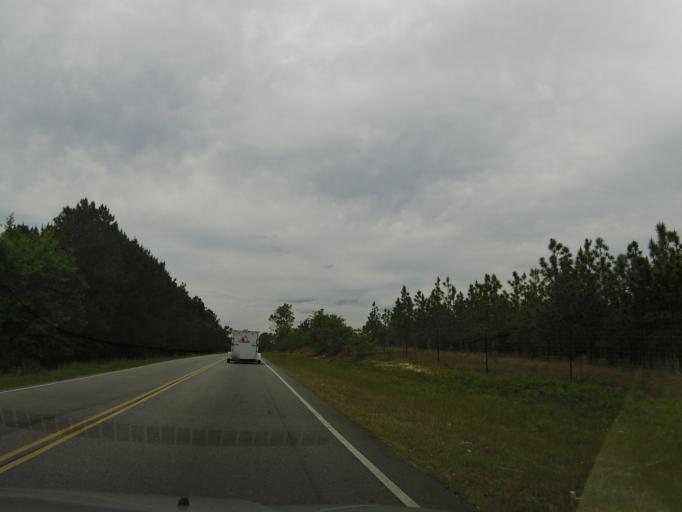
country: US
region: Georgia
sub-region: Candler County
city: Metter
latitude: 32.3980
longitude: -82.1837
